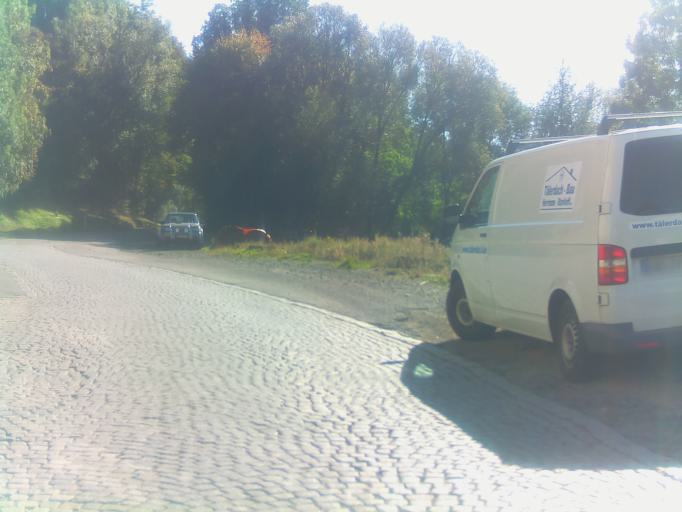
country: DE
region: Thuringia
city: Ottendorf
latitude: 50.8261
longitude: 11.8228
